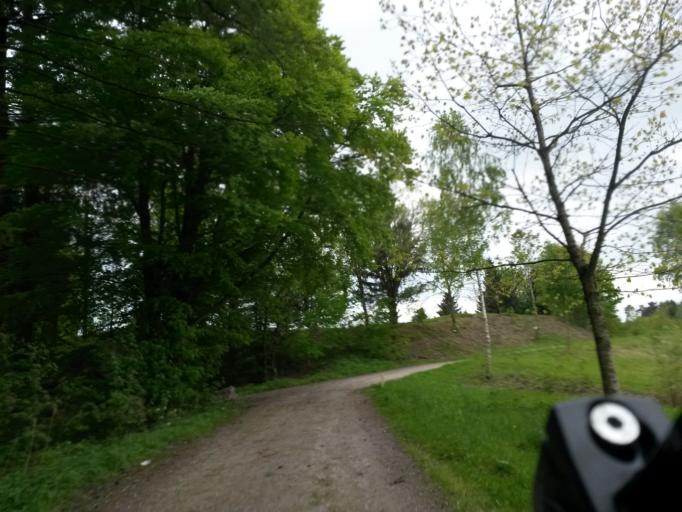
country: DE
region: Baden-Wuerttemberg
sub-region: Tuebingen Region
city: Bad Waldsee
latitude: 47.9366
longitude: 9.7836
